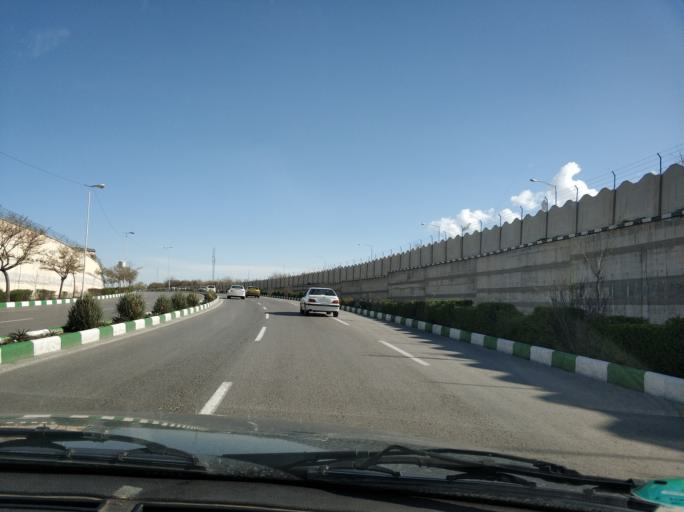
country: IR
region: Razavi Khorasan
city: Mashhad
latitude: 36.3041
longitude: 59.6280
